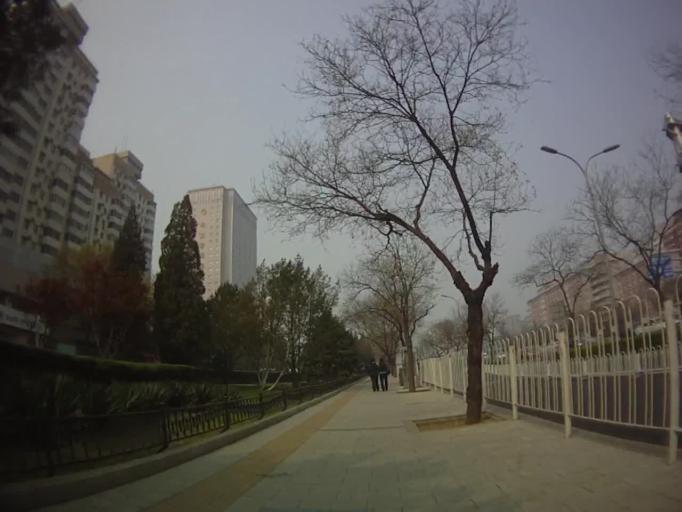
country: CN
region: Beijing
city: Chaowai
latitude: 39.9069
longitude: 116.4345
